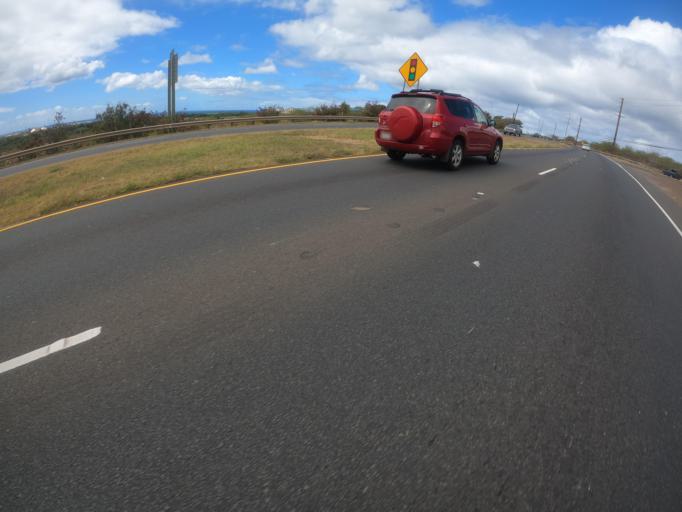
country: US
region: Hawaii
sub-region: Honolulu County
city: Makakilo City
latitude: 21.3410
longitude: -158.1036
